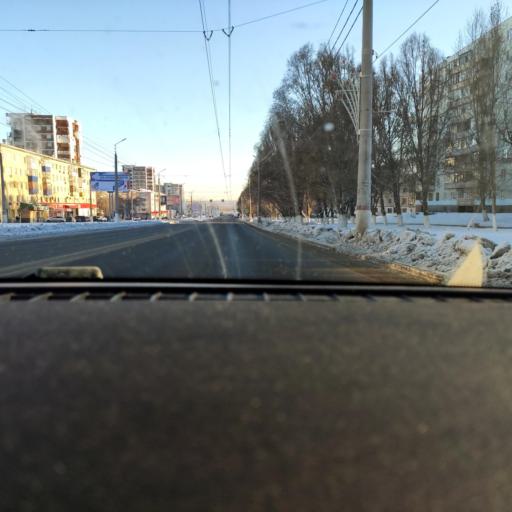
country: RU
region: Samara
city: Novokuybyshevsk
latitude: 53.0917
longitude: 49.9834
